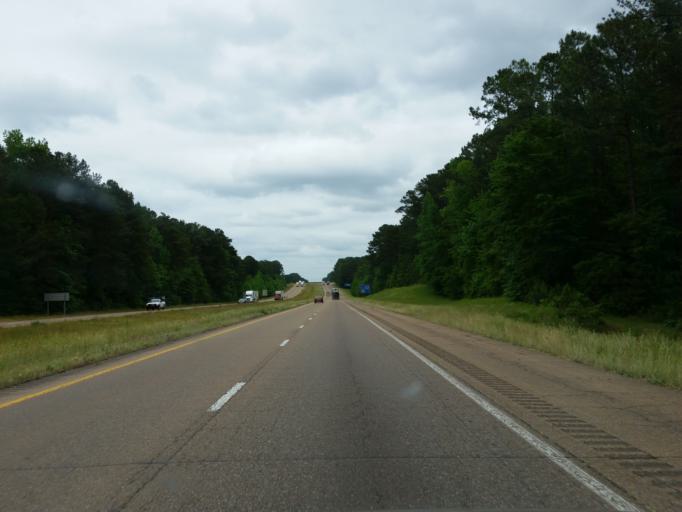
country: US
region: Mississippi
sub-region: Lauderdale County
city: Marion
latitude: 32.3917
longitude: -88.5930
